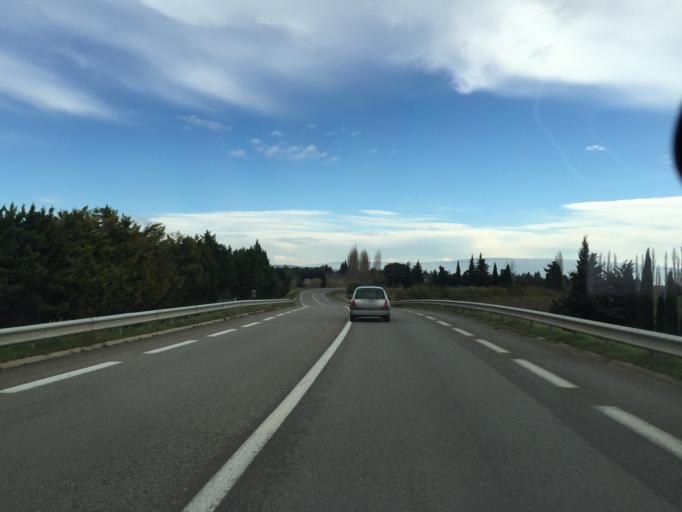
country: FR
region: Provence-Alpes-Cote d'Azur
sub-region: Departement du Vaucluse
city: L'Isle-sur-la-Sorgue
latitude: 43.9112
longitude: 5.0324
